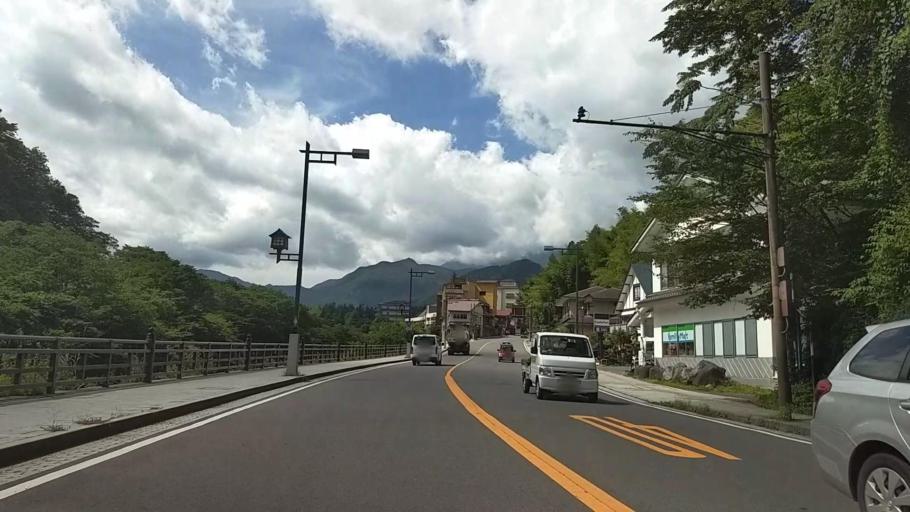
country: JP
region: Tochigi
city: Nikko
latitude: 36.7530
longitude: 139.6026
